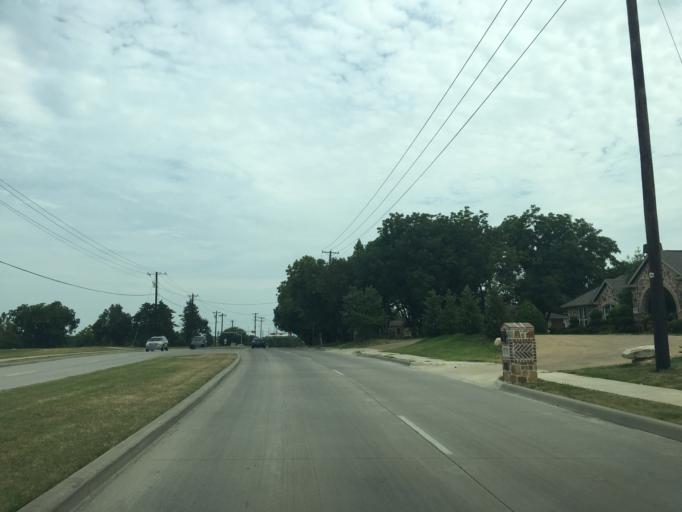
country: US
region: Texas
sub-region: Collin County
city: Wylie
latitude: 33.0039
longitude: -96.5220
